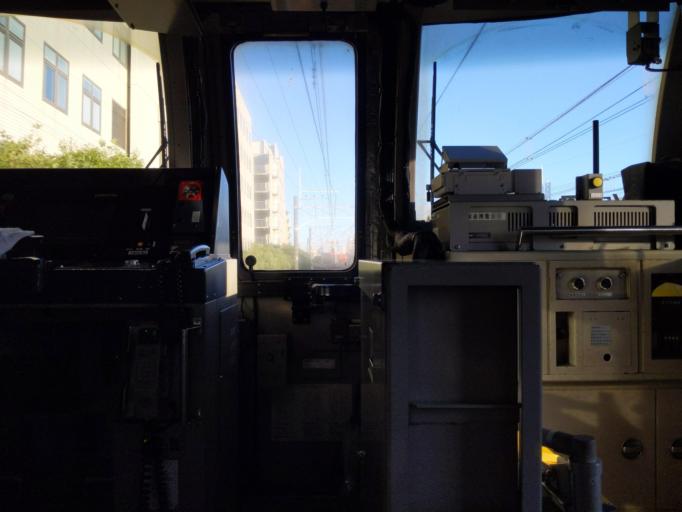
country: JP
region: Chiba
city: Funabashi
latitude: 35.7035
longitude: 139.9683
